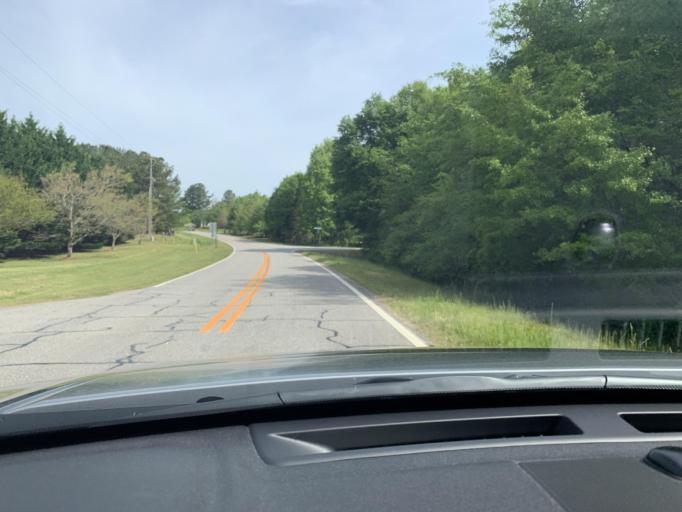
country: US
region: Georgia
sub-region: Oconee County
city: Watkinsville
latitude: 33.8392
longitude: -83.4871
